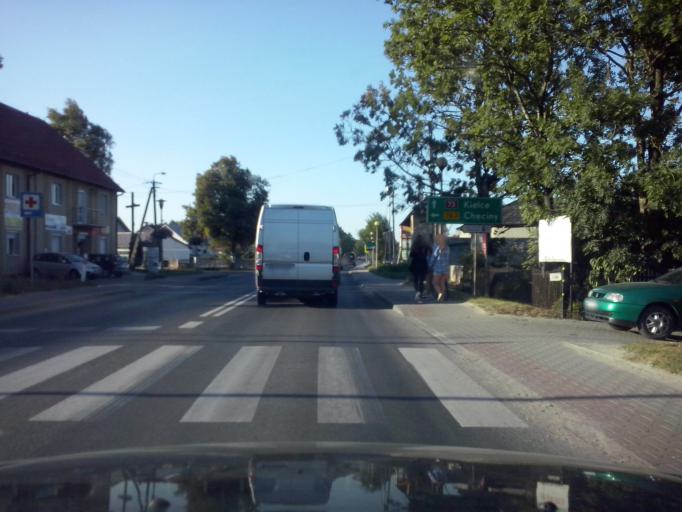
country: PL
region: Swietokrzyskie
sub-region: Powiat kielecki
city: Morawica
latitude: 50.7513
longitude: 20.6183
